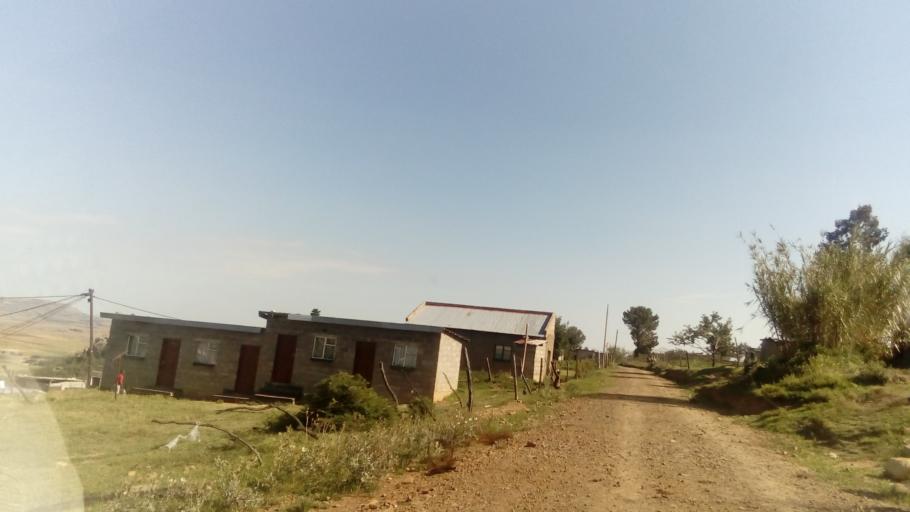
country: LS
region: Berea
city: Teyateyaneng
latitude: -29.1414
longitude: 27.7482
